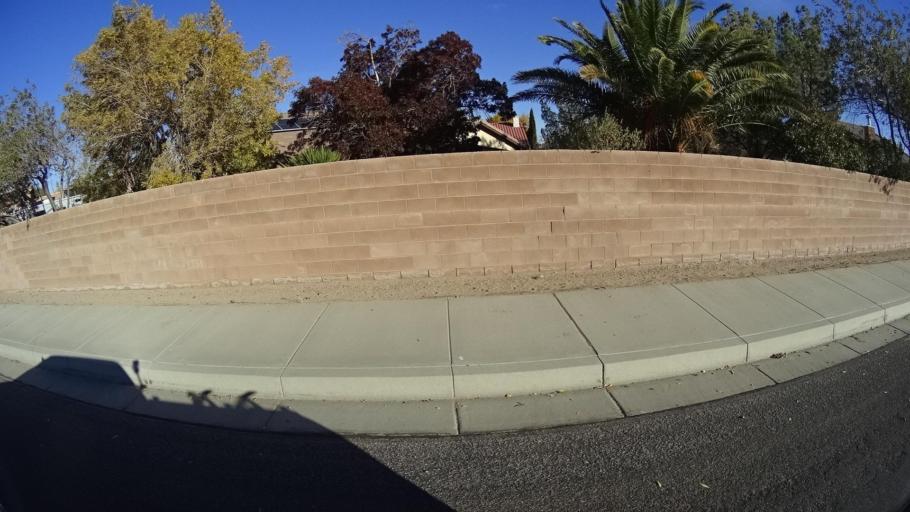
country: US
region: California
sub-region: Kern County
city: Ridgecrest
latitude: 35.6421
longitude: -117.6965
